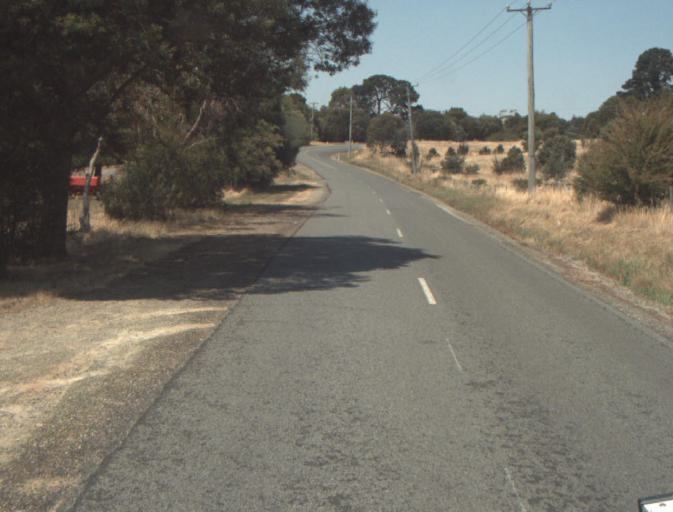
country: AU
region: Tasmania
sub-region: Launceston
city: Newstead
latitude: -41.4926
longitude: 147.2073
